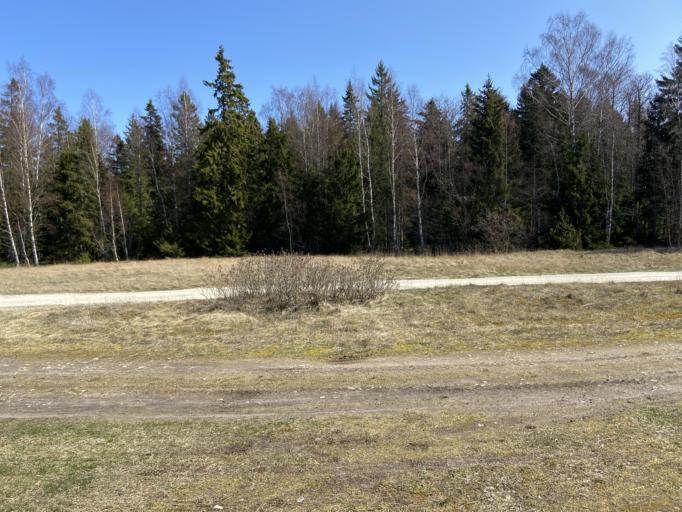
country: EE
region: Harju
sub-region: Kuusalu vald
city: Kuusalu
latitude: 59.6439
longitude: 25.5048
